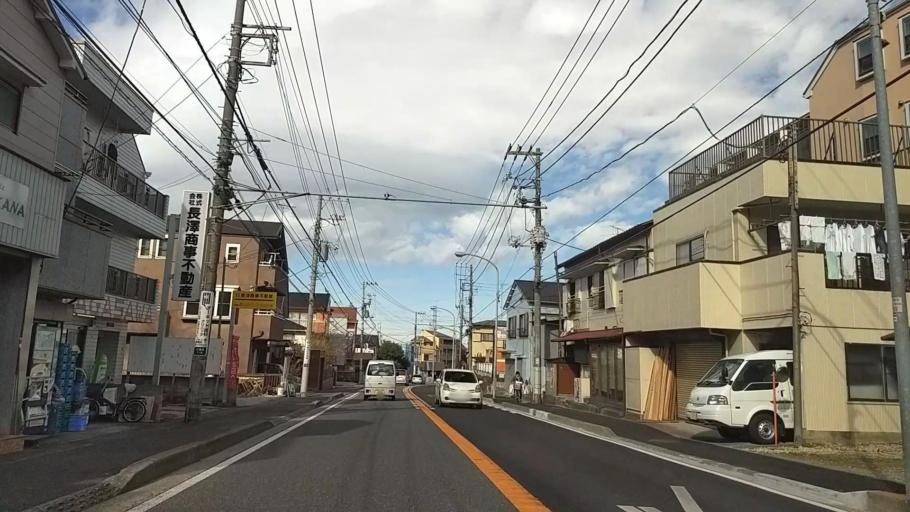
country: JP
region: Kanagawa
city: Yokohama
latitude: 35.5239
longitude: 139.6330
